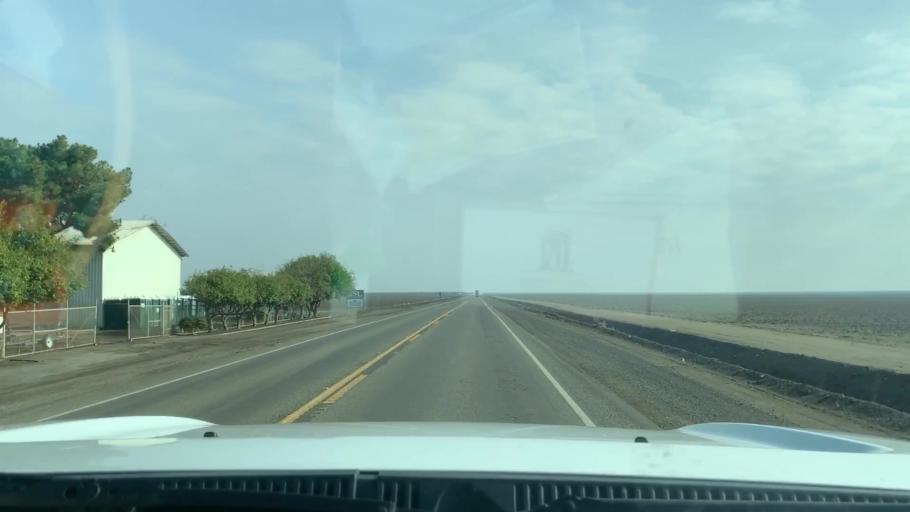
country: US
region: California
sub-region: Fresno County
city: Huron
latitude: 36.2553
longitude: -120.0832
